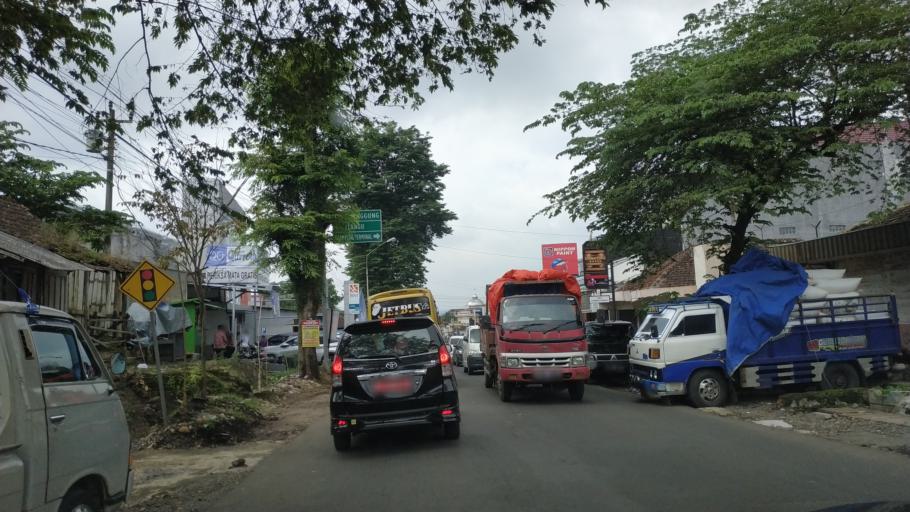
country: ID
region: Central Java
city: Weleri
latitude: -7.0887
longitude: 110.0477
